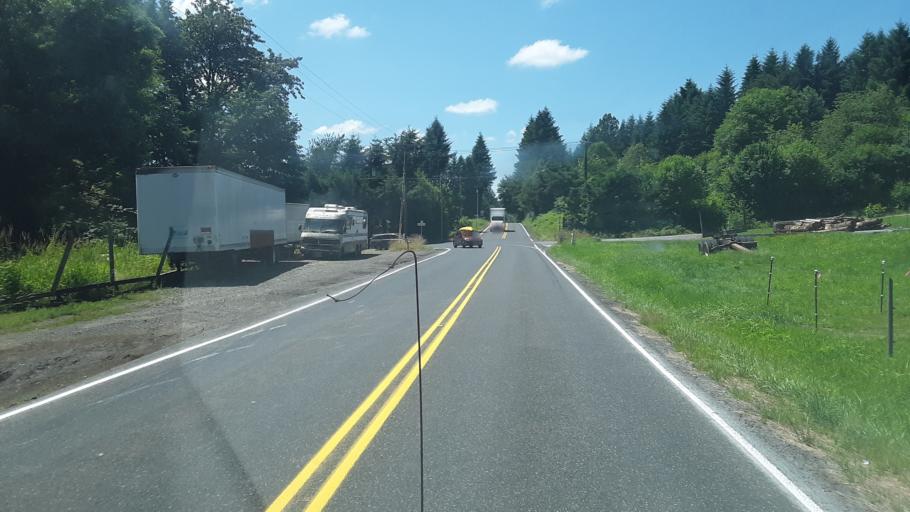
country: US
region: Washington
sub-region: Clark County
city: Amboy
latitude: 45.9172
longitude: -122.4456
